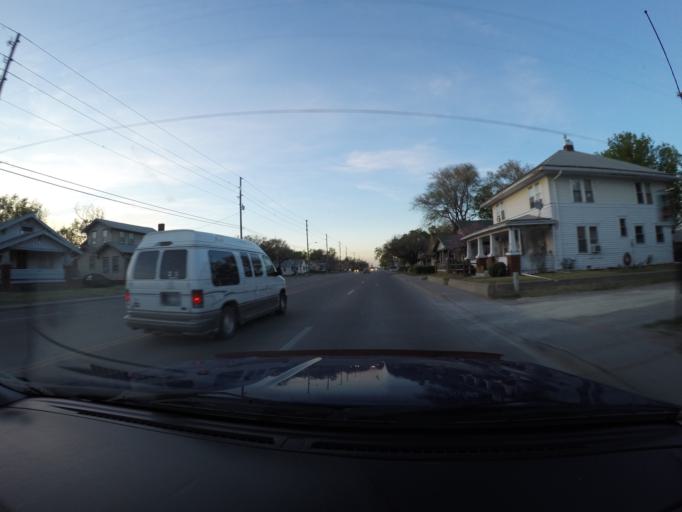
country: US
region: Kansas
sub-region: Saline County
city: Salina
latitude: 38.8410
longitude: -97.5940
